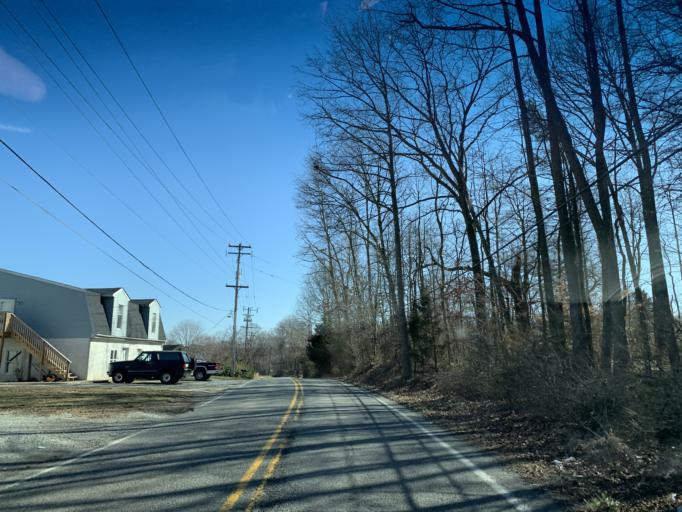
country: US
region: Maryland
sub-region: Cecil County
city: North East
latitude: 39.5994
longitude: -75.9596
